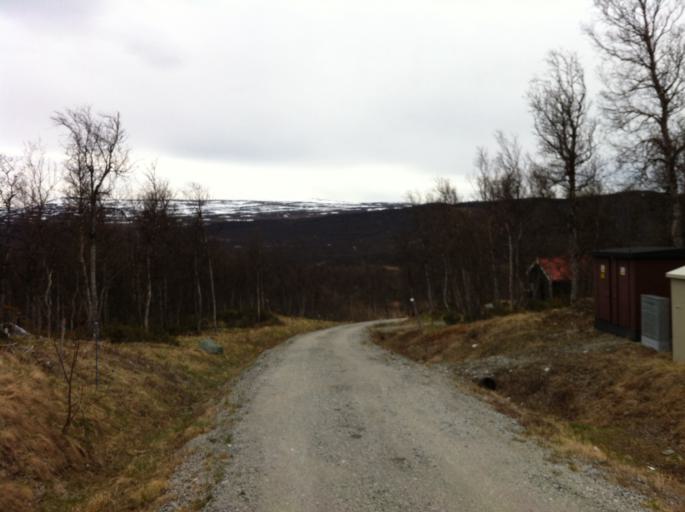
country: NO
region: Sor-Trondelag
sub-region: Tydal
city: Aas
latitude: 62.5522
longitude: 12.3122
